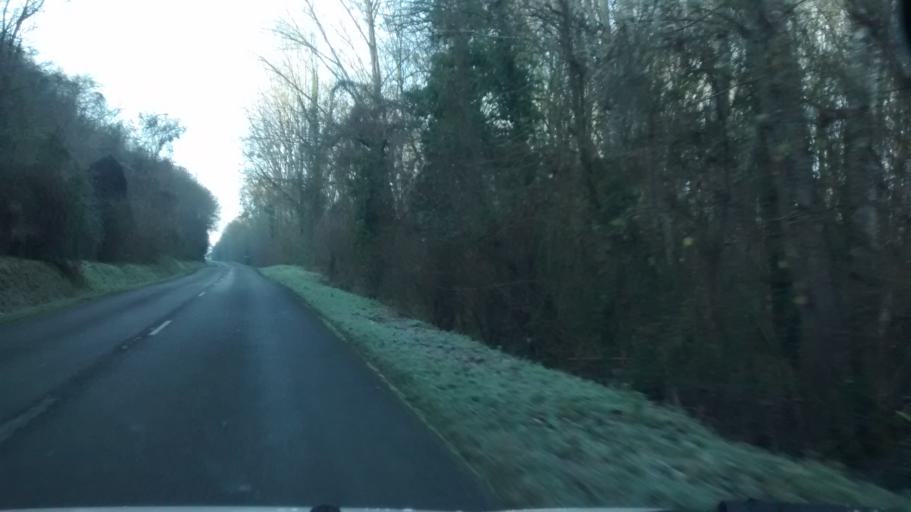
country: FR
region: Centre
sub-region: Departement d'Indre-et-Loire
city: Villandry
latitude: 47.3448
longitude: 0.5257
